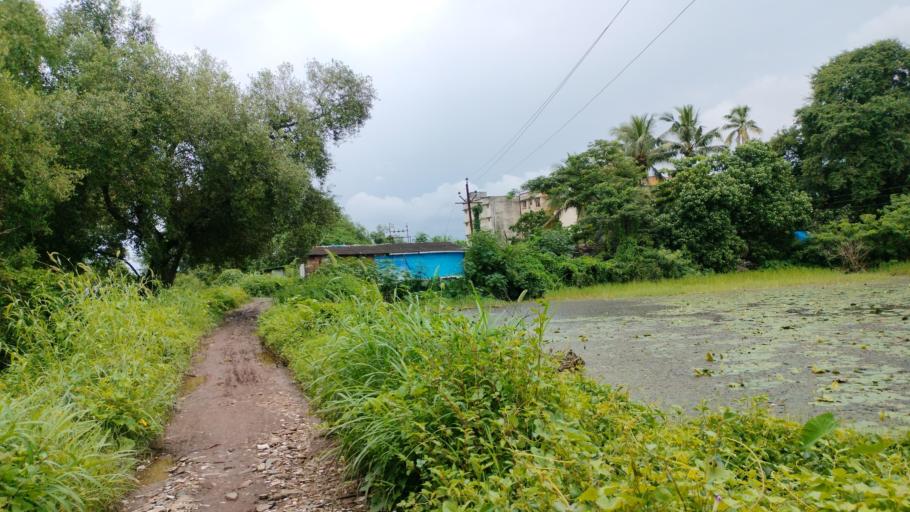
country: IN
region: Maharashtra
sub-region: Thane
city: Virar
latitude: 19.4665
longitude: 72.7758
